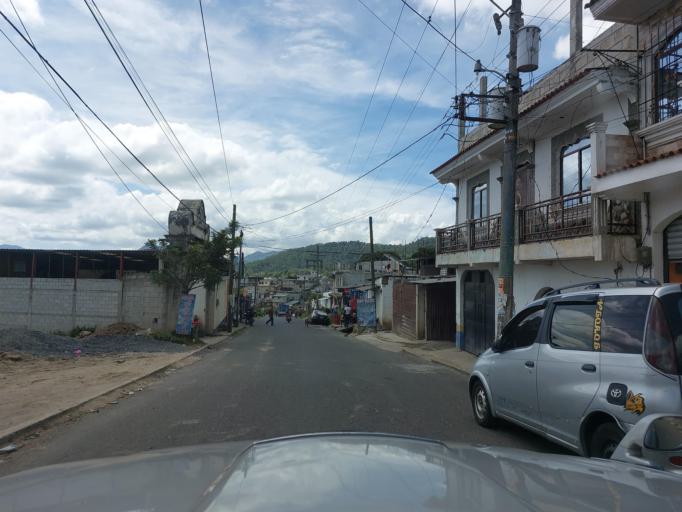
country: GT
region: Chimaltenango
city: San Andres Itzapa
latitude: 14.6214
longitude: -90.8378
